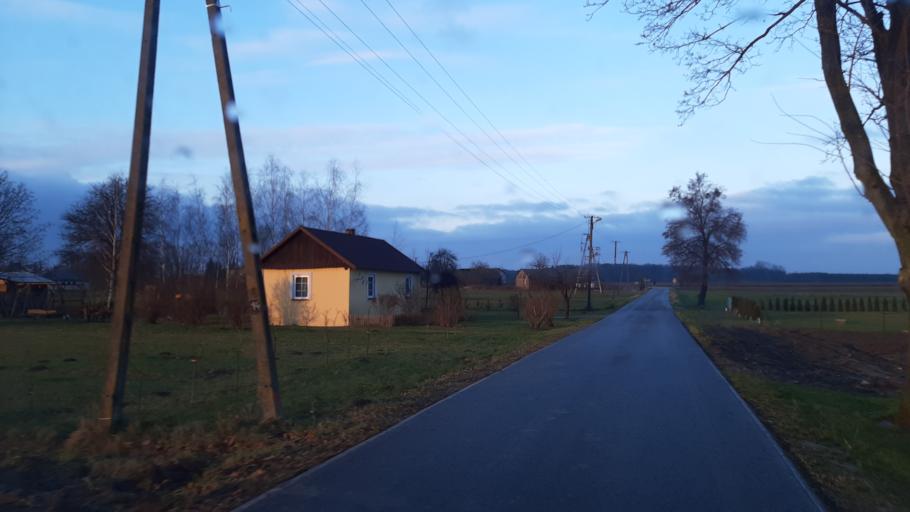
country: PL
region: Lublin Voivodeship
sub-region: Powiat lubelski
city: Garbow
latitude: 51.3781
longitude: 22.4013
